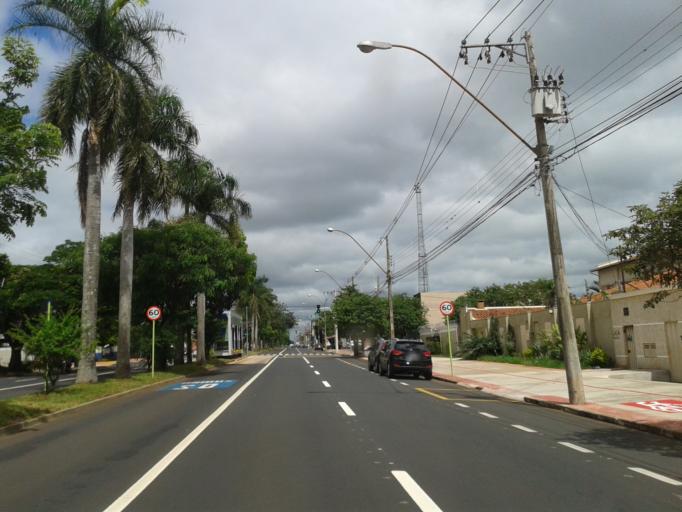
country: BR
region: Minas Gerais
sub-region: Uberaba
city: Uberaba
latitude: -19.7453
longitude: -47.9524
